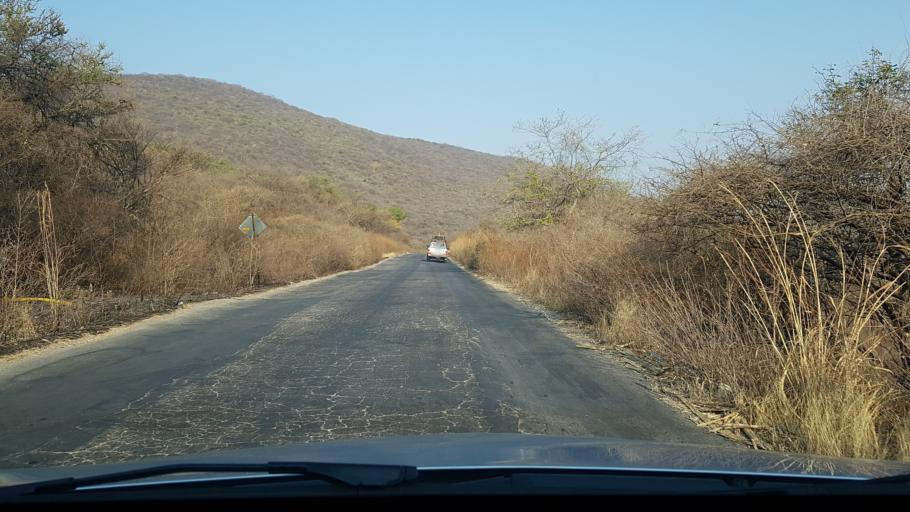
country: MX
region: Morelos
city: Tlaltizapan
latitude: 18.6636
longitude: -99.0471
